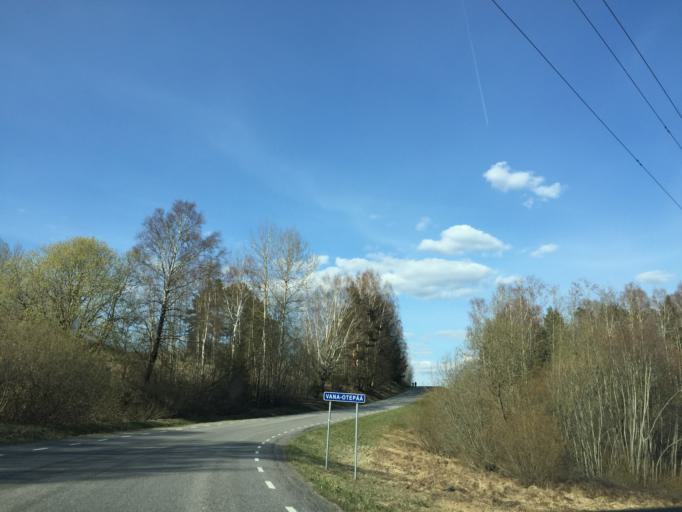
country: EE
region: Tartu
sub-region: Elva linn
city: Elva
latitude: 58.0700
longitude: 26.5163
